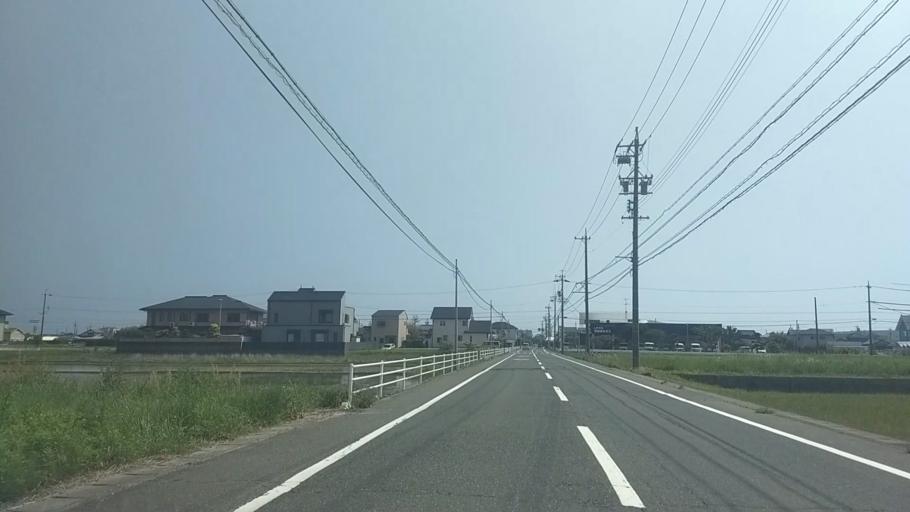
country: JP
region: Shizuoka
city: Hamamatsu
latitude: 34.6756
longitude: 137.7166
